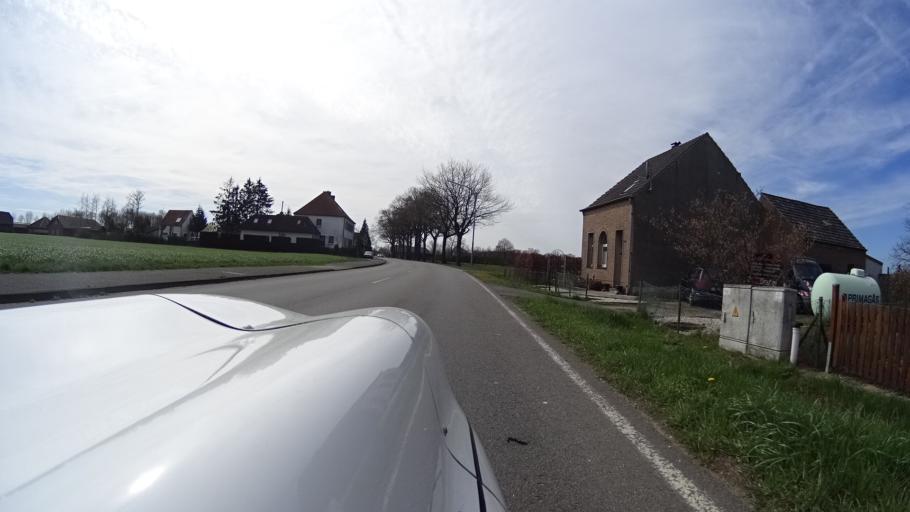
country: DE
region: North Rhine-Westphalia
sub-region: Regierungsbezirk Dusseldorf
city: Kevelaer
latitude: 51.5791
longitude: 6.2263
